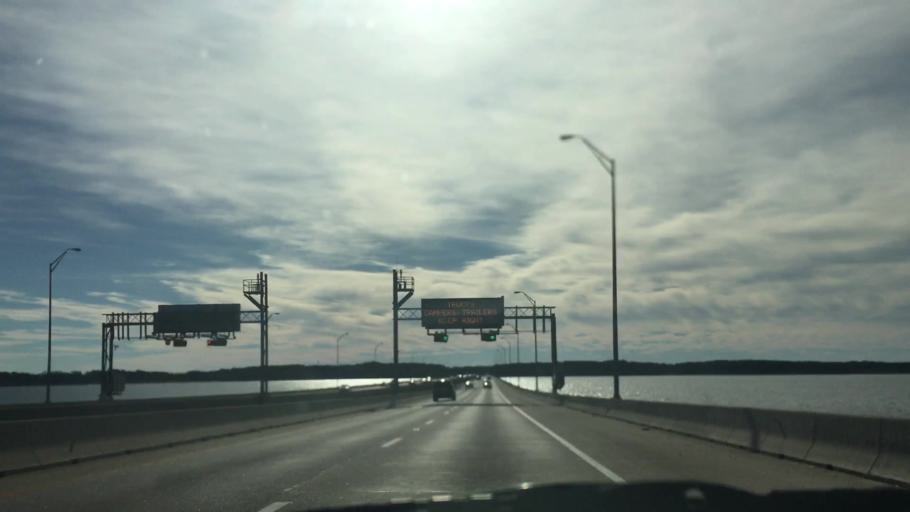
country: US
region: Virginia
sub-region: City of Newport News
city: Newport News
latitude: 36.9137
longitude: -76.4129
